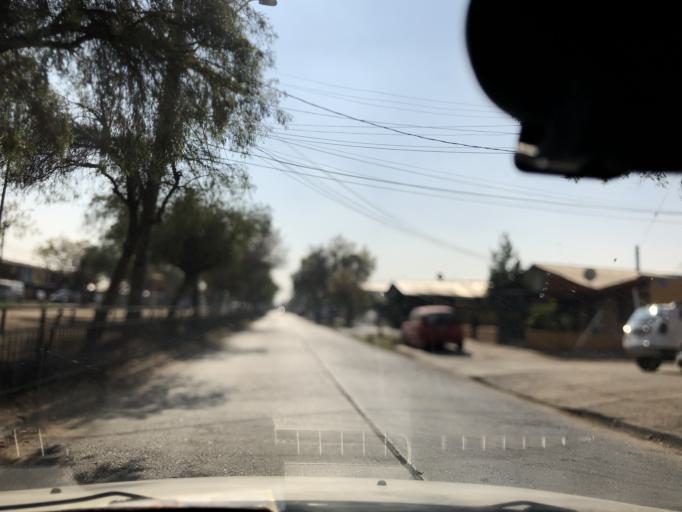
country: CL
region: Santiago Metropolitan
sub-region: Provincia de Cordillera
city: Puente Alto
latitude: -33.6224
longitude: -70.5901
